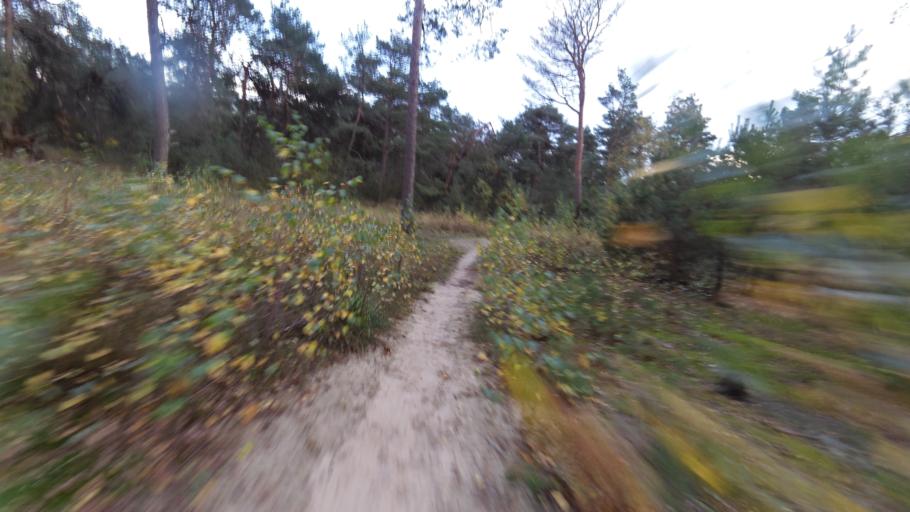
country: NL
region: Gelderland
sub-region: Gemeente Nunspeet
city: Nunspeet
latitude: 52.3882
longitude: 5.8383
